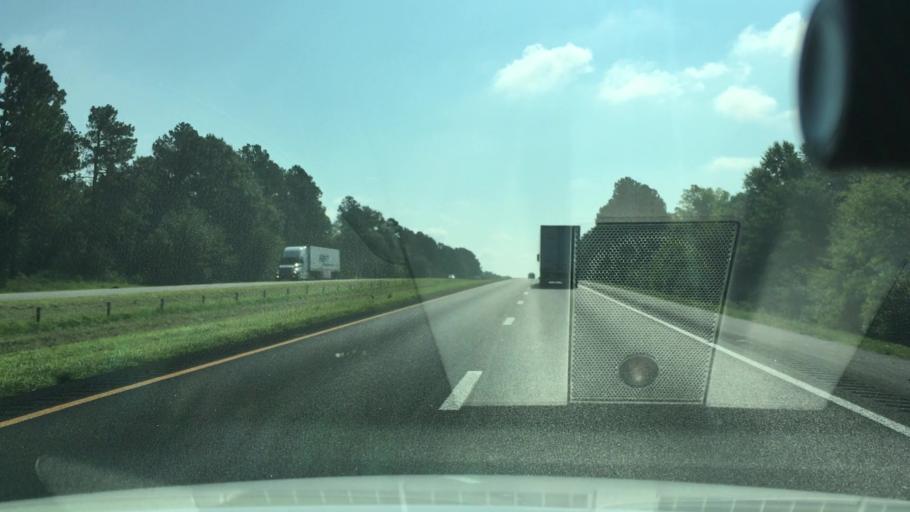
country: US
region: South Carolina
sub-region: Aiken County
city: Graniteville
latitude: 33.6348
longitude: -81.7689
